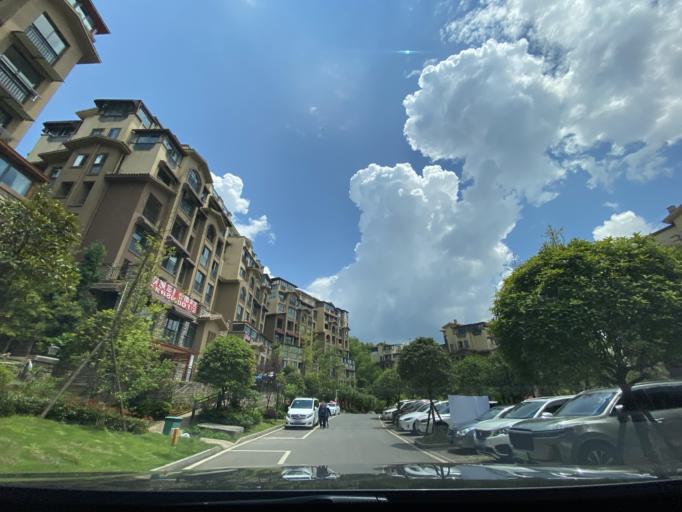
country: CN
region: Guizhou Sheng
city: Changqi
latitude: 28.5364
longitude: 105.9732
